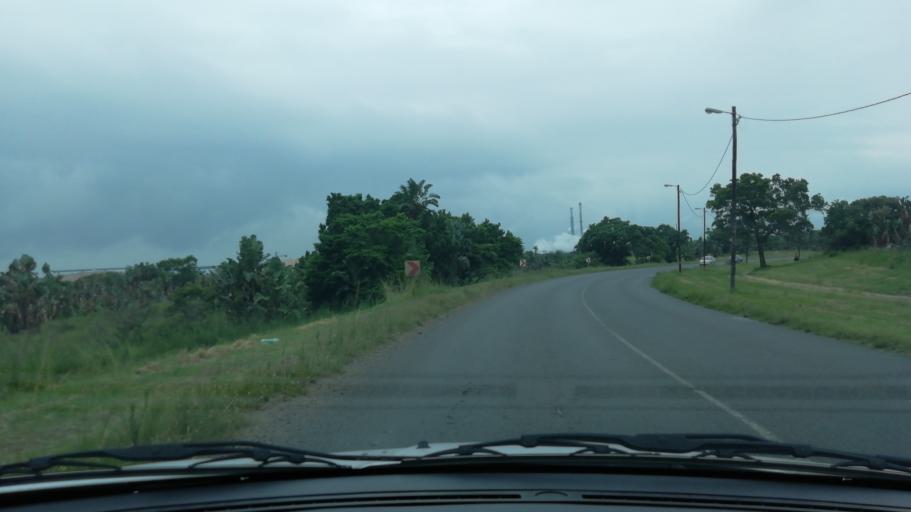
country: ZA
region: KwaZulu-Natal
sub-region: uThungulu District Municipality
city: Richards Bay
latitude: -28.7614
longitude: 32.0429
